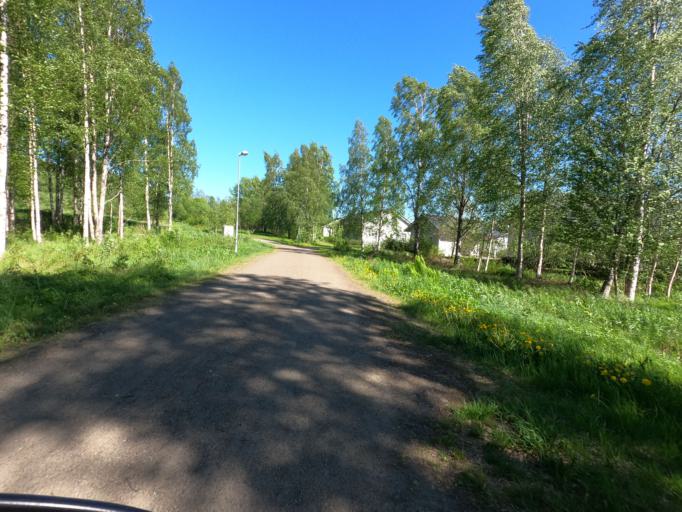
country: FI
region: North Karelia
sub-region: Joensuu
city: Joensuu
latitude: 62.6045
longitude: 29.8241
